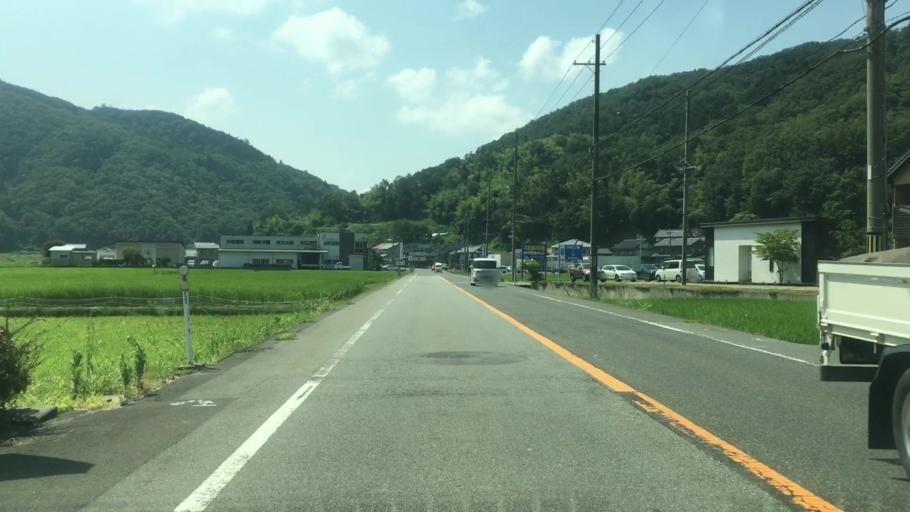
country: JP
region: Hyogo
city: Toyooka
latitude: 35.5659
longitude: 134.7901
